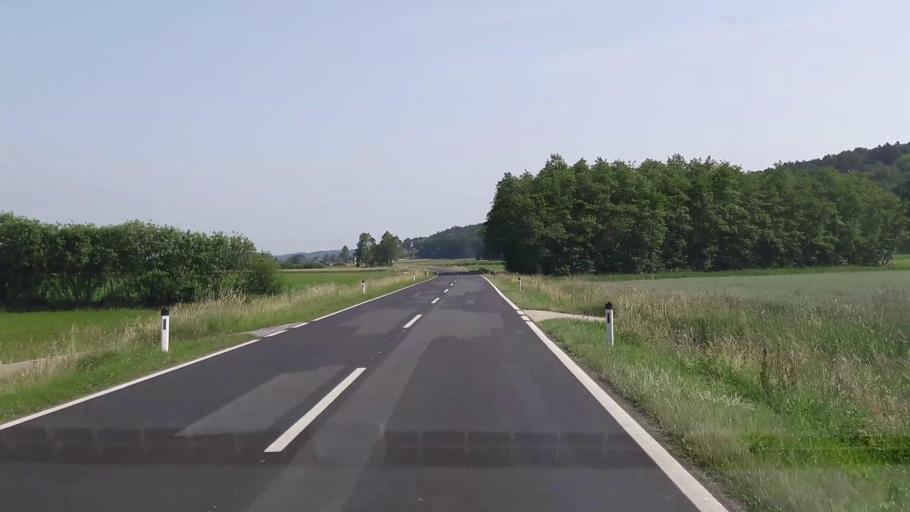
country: AT
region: Burgenland
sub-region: Politischer Bezirk Jennersdorf
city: Deutsch Kaltenbrunn
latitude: 47.1060
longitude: 16.1106
